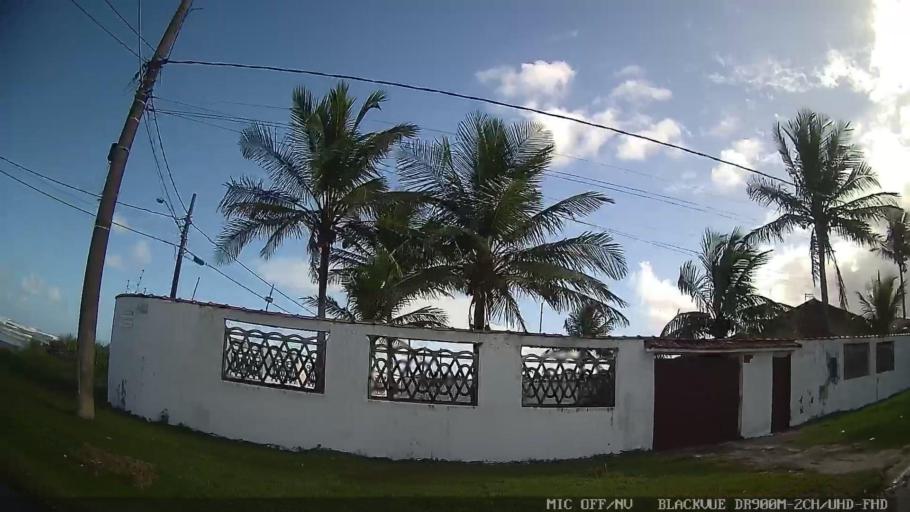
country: BR
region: Sao Paulo
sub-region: Itanhaem
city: Itanhaem
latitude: -24.1533
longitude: -46.7279
